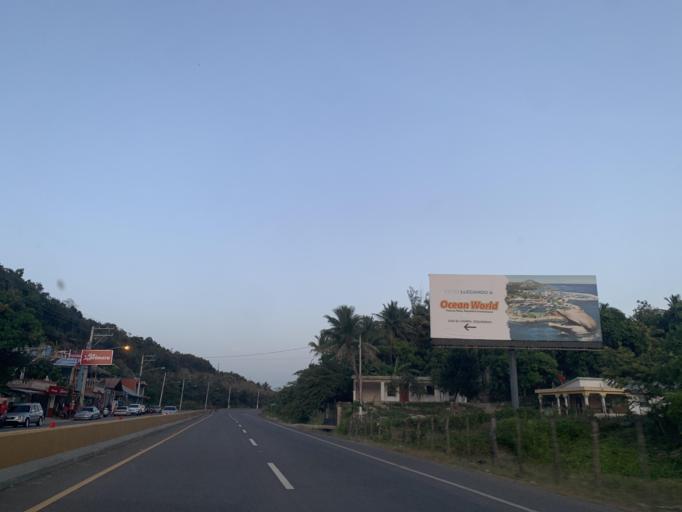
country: DO
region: Puerto Plata
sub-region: Puerto Plata
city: Puerto Plata
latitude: 19.8206
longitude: -70.7376
